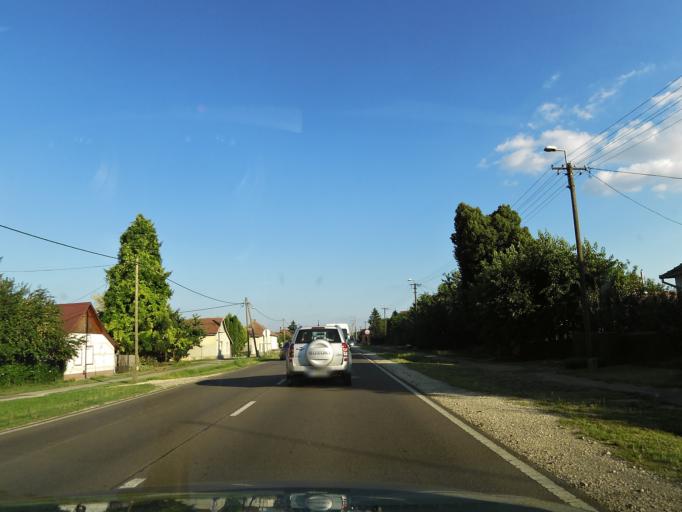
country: HU
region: Jasz-Nagykun-Szolnok
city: Rakocziujfalu
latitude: 47.0630
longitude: 20.2591
